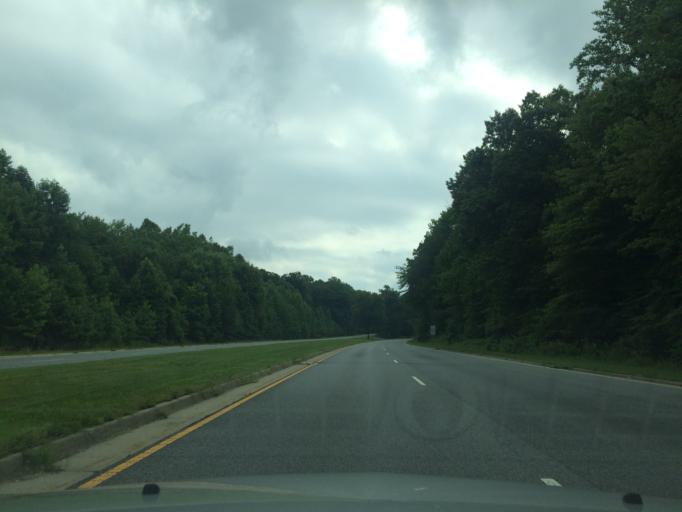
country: US
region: Maryland
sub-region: Prince George's County
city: Morningside
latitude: 38.8362
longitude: -76.8978
